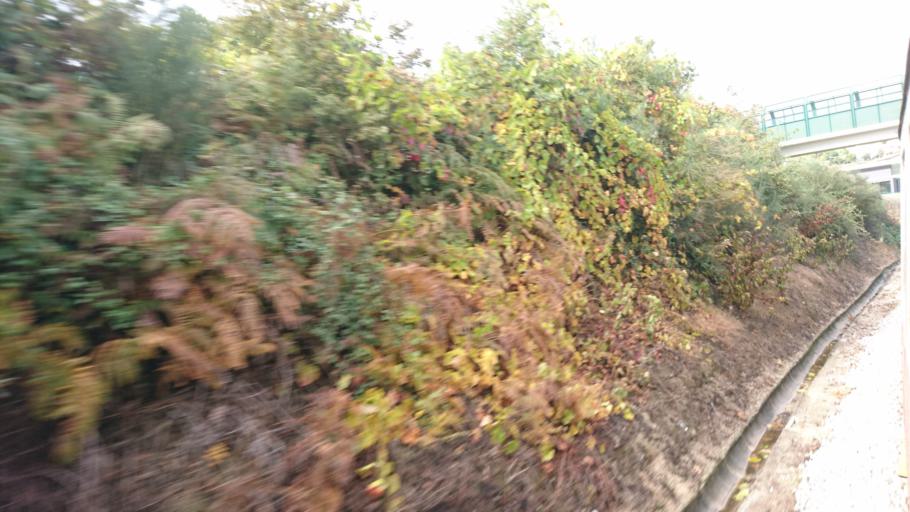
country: PT
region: Porto
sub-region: Marco de Canaveses
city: Marco de Canavezes
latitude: 41.1845
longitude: -8.1396
